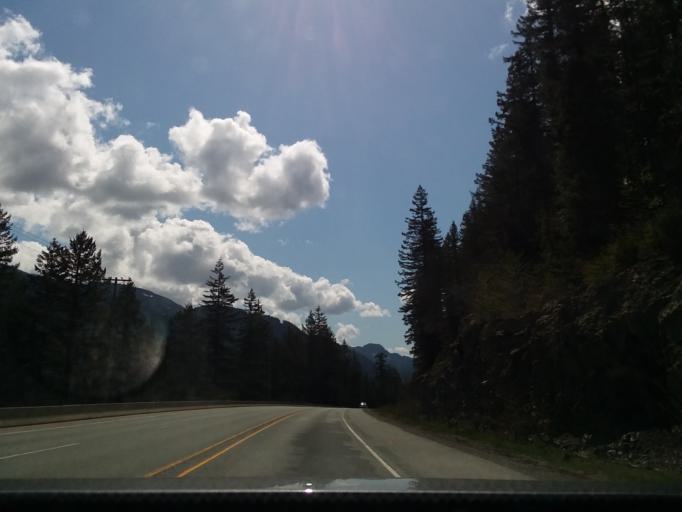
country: CA
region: British Columbia
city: Whistler
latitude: 50.0178
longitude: -123.1229
